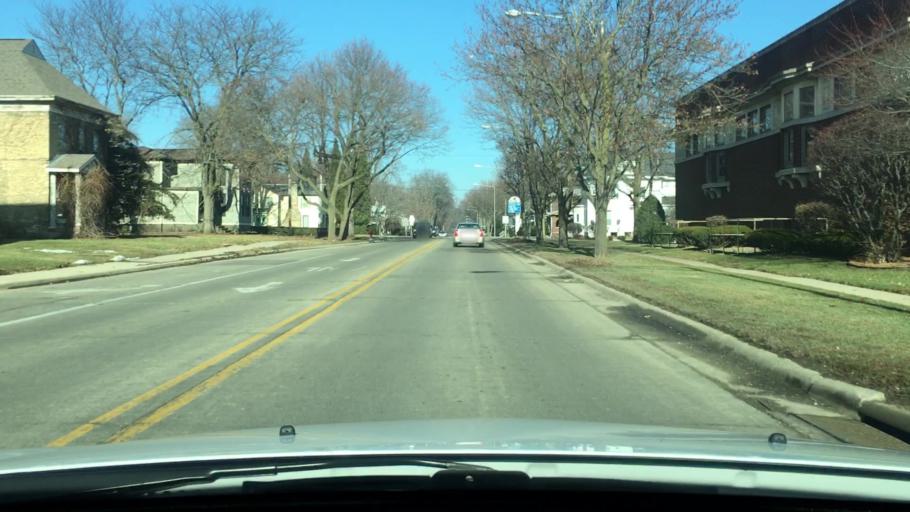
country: US
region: Illinois
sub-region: Ogle County
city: Rochelle
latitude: 41.9229
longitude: -89.0688
